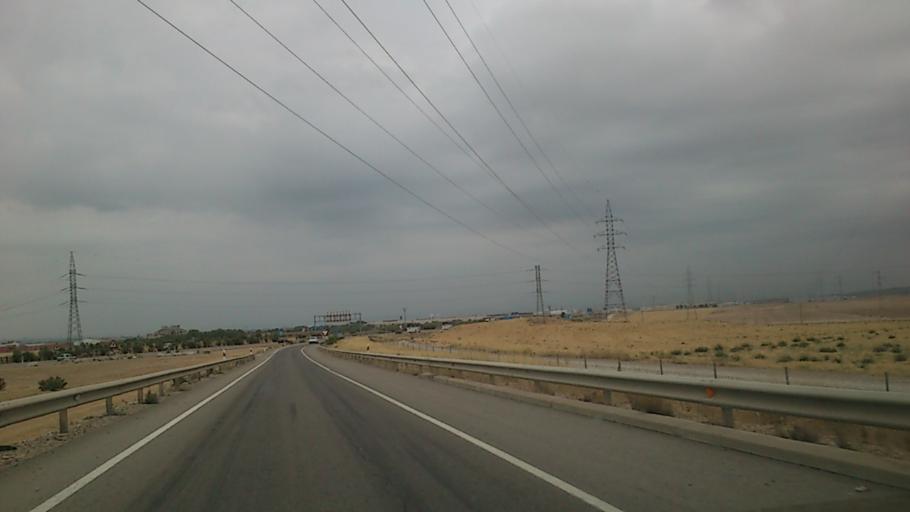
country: ES
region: Aragon
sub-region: Provincia de Zaragoza
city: Villanueva de Gallego
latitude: 41.7796
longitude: -0.8340
